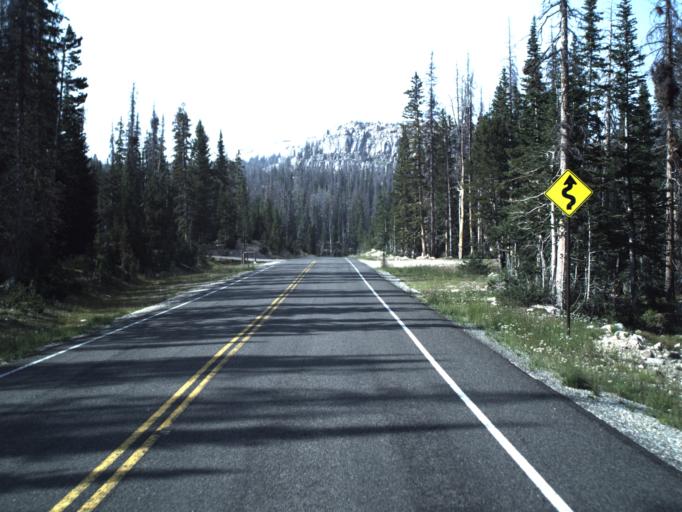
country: US
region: Utah
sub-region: Summit County
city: Kamas
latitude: 40.7159
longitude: -110.8765
